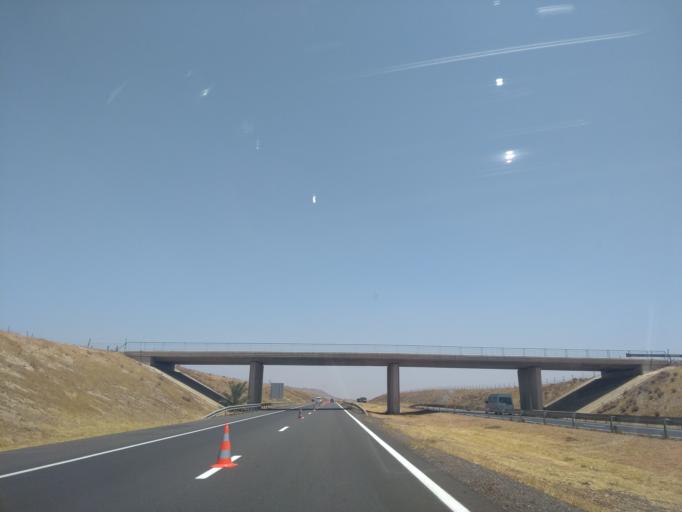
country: MA
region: Marrakech-Tensift-Al Haouz
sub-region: Kelaa-Des-Sraghna
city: Sidi Abdallah
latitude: 32.4368
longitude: -7.9316
